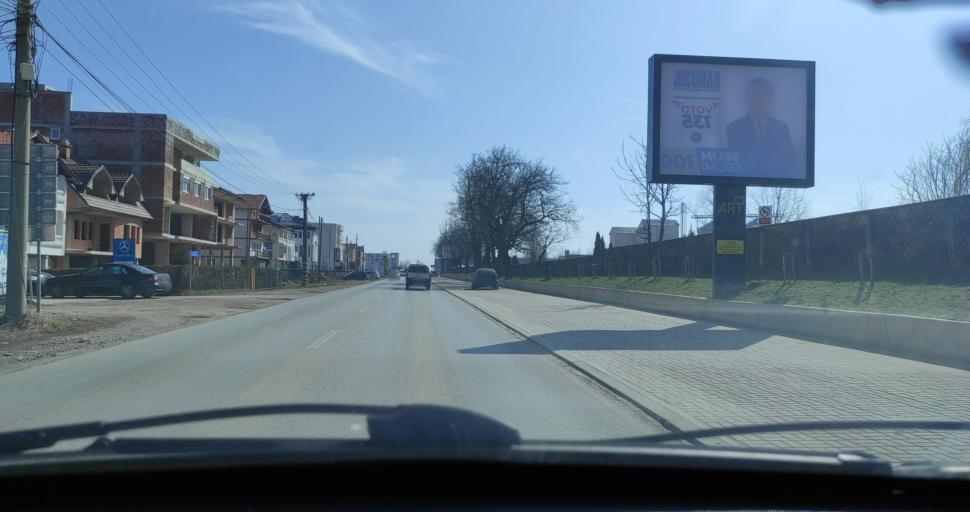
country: XK
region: Pec
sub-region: Komuna e Pejes
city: Peje
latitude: 42.6396
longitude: 20.2959
